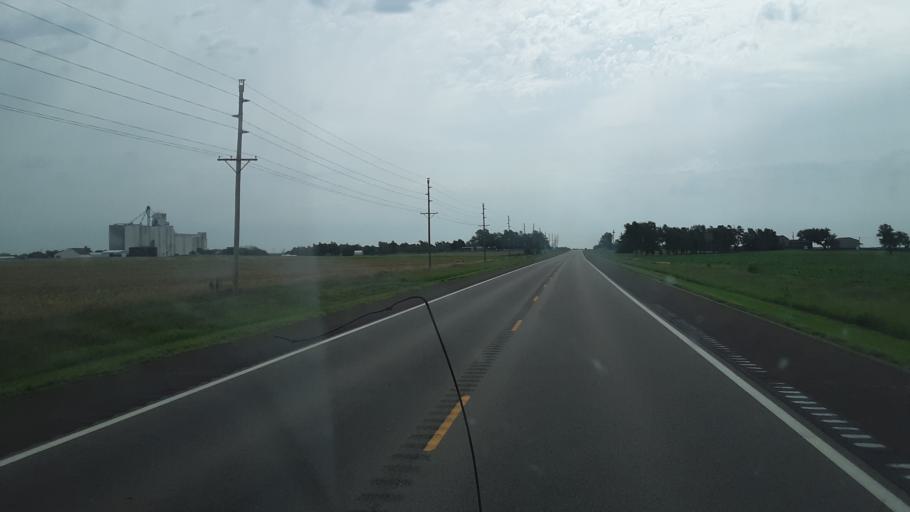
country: US
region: Kansas
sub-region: Stafford County
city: Stafford
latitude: 37.9551
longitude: -98.5035
